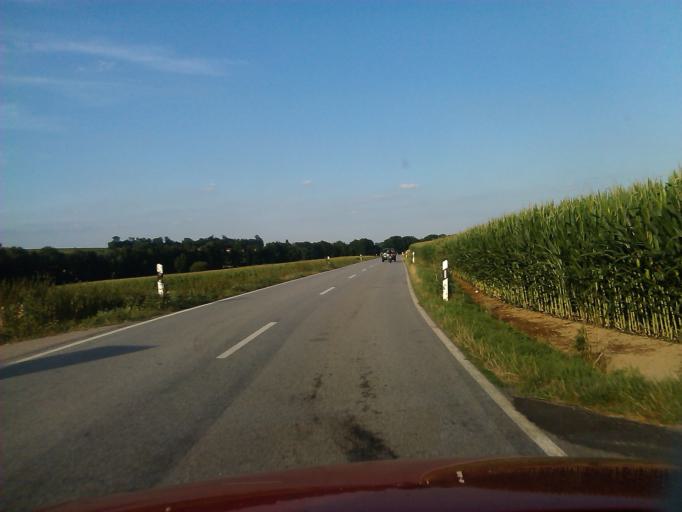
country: DE
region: Baden-Wuerttemberg
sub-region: Regierungsbezirk Stuttgart
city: Schwaigern
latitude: 49.1362
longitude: 9.0262
